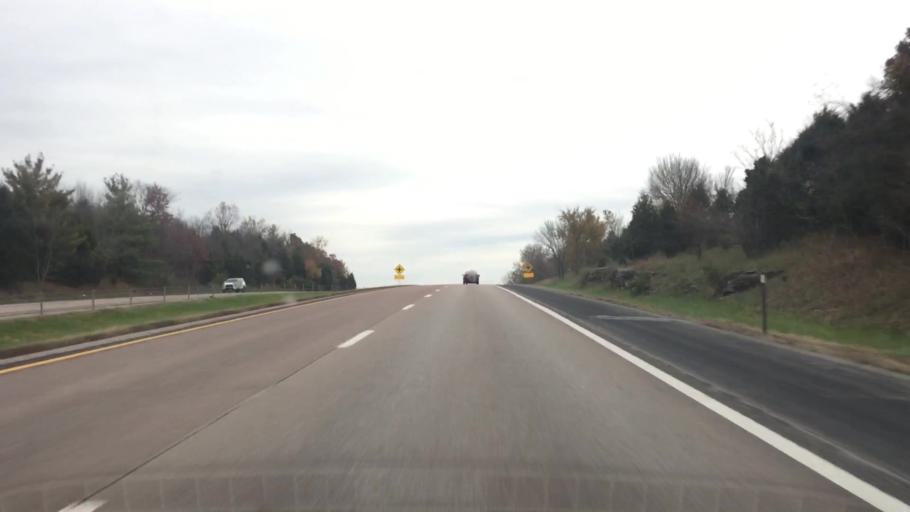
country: US
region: Missouri
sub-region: Boone County
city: Ashland
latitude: 38.6929
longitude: -92.2548
